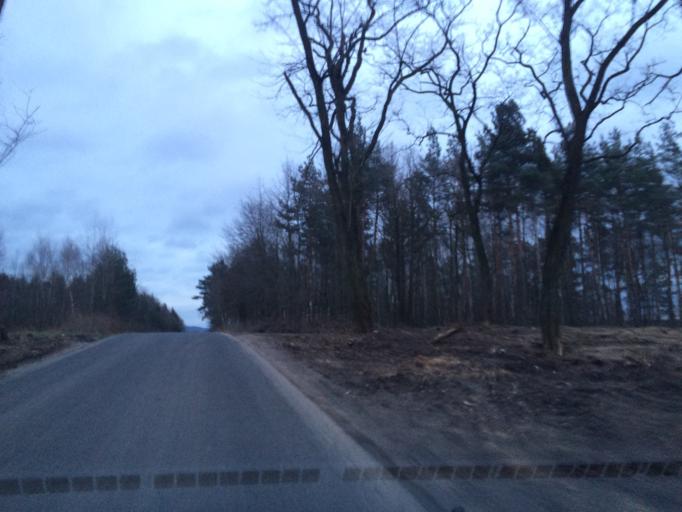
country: PL
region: Lower Silesian Voivodeship
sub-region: Powiat boleslawiecki
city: Nowogrodziec
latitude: 51.1977
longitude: 15.4554
